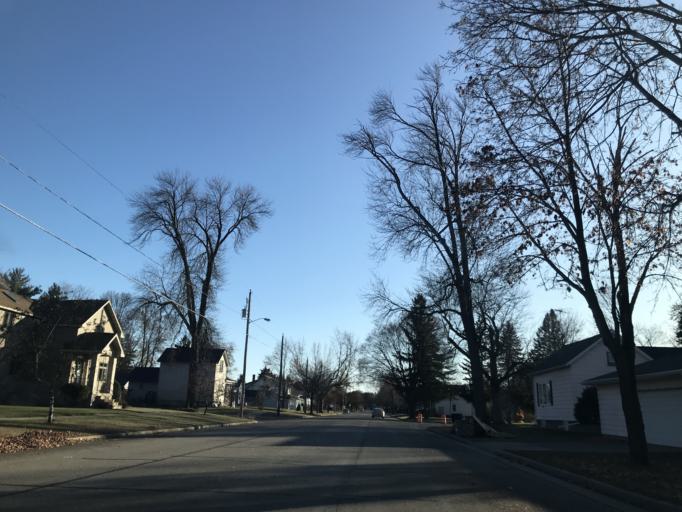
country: US
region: Wisconsin
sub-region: Marinette County
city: Peshtigo
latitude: 45.0570
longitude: -87.7419
